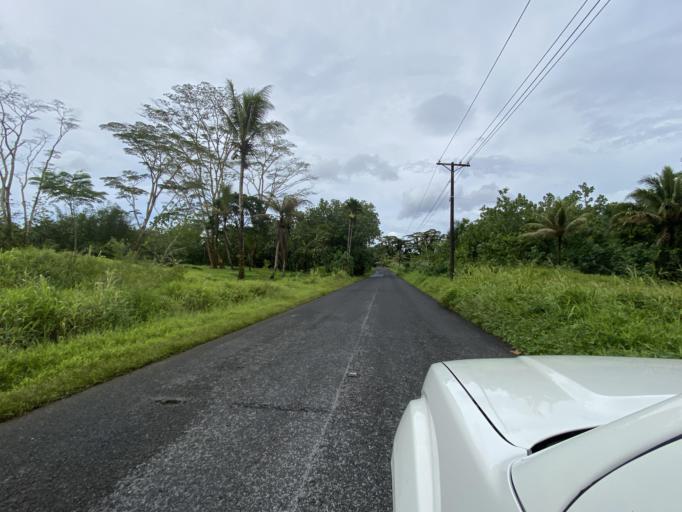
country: FM
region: Pohnpei
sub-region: Sokehs Municipality
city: Palikir - National Government Center
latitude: 6.9198
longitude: 158.1621
